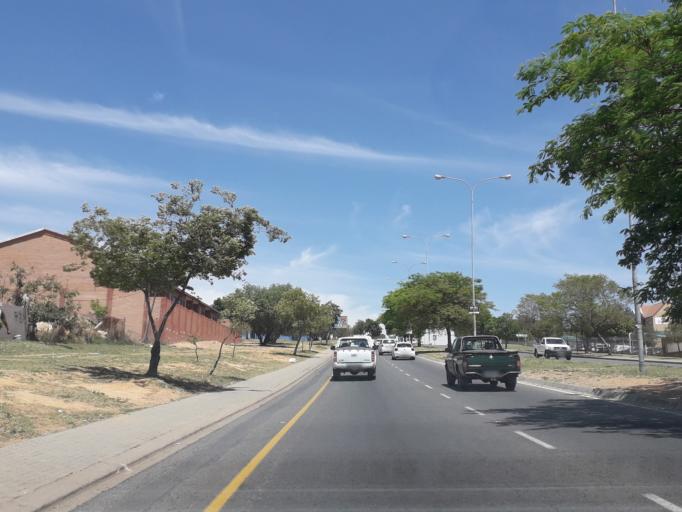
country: ZA
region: Gauteng
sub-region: City of Johannesburg Metropolitan Municipality
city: Modderfontein
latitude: -26.0907
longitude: 28.0905
